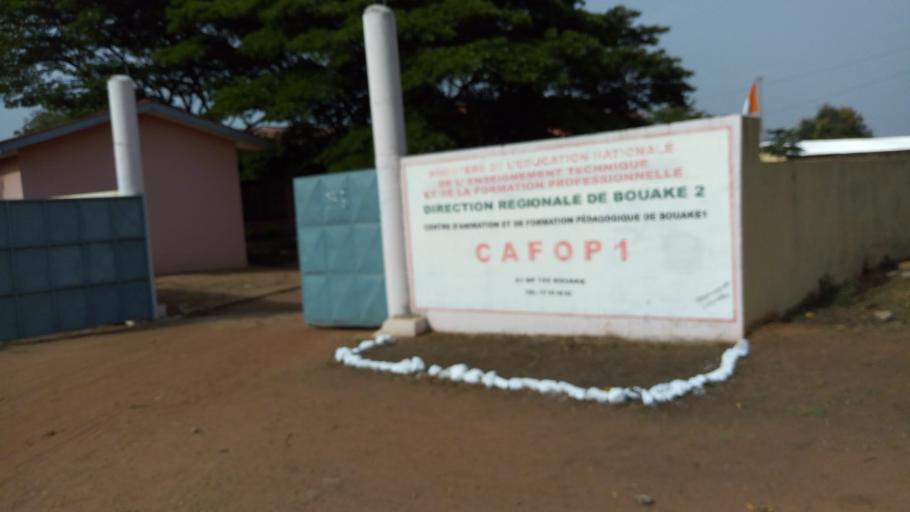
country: CI
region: Vallee du Bandama
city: Bouake
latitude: 7.7017
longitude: -5.0333
